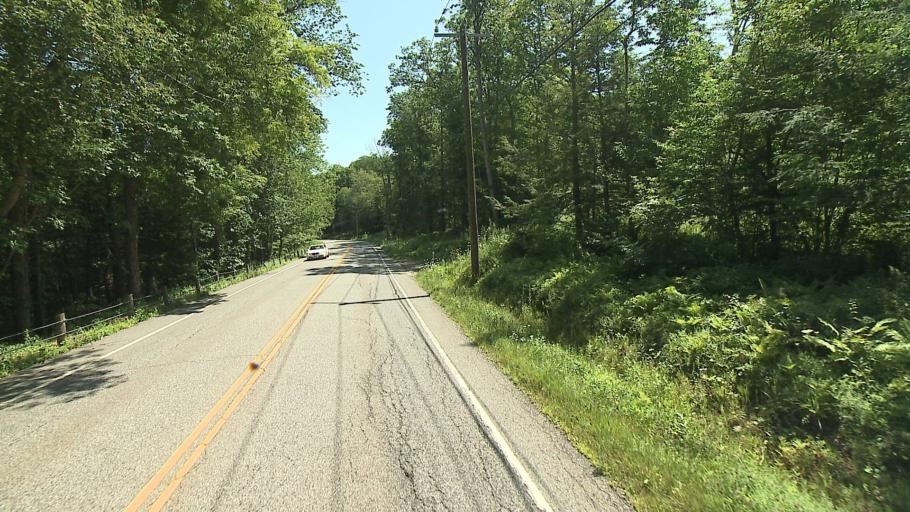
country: US
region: Connecticut
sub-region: Litchfield County
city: Kent
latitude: 41.8222
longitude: -73.3924
